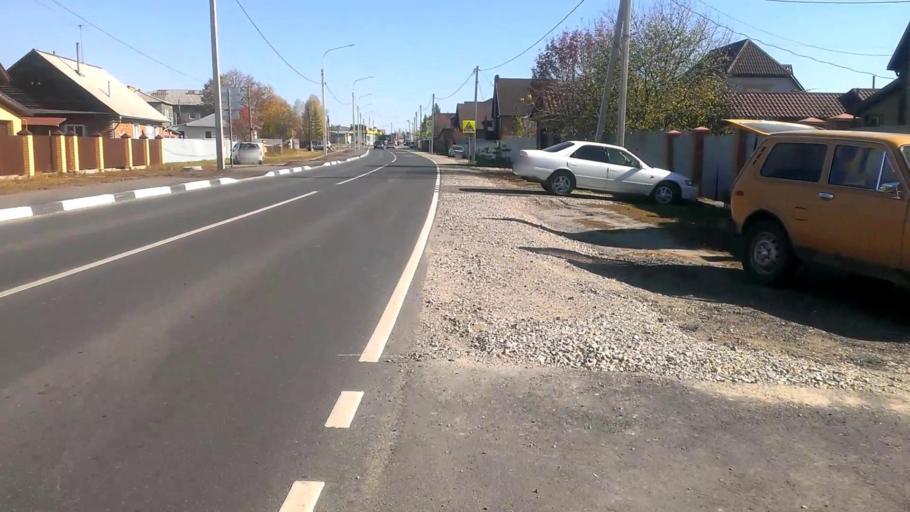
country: RU
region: Altai Krai
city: Sannikovo
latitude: 53.3173
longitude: 83.9507
